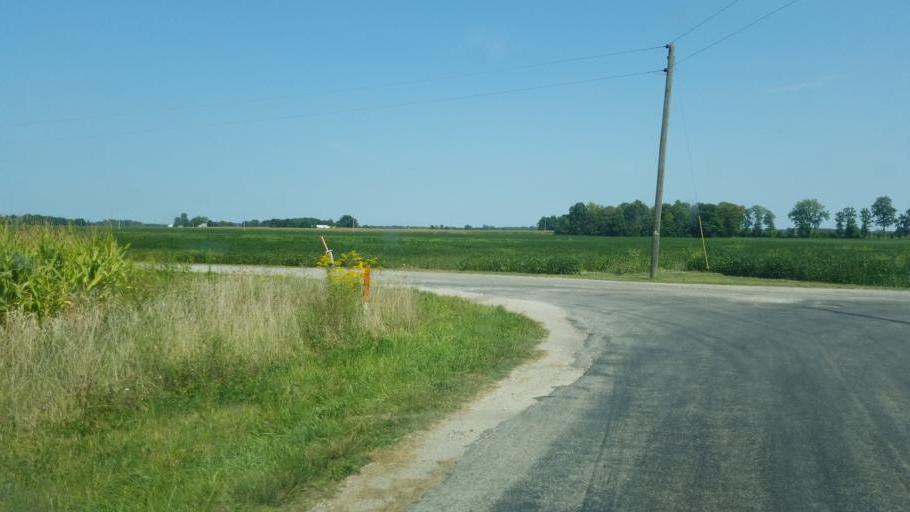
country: US
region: Ohio
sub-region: Richland County
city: Shelby
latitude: 40.9165
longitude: -82.7980
